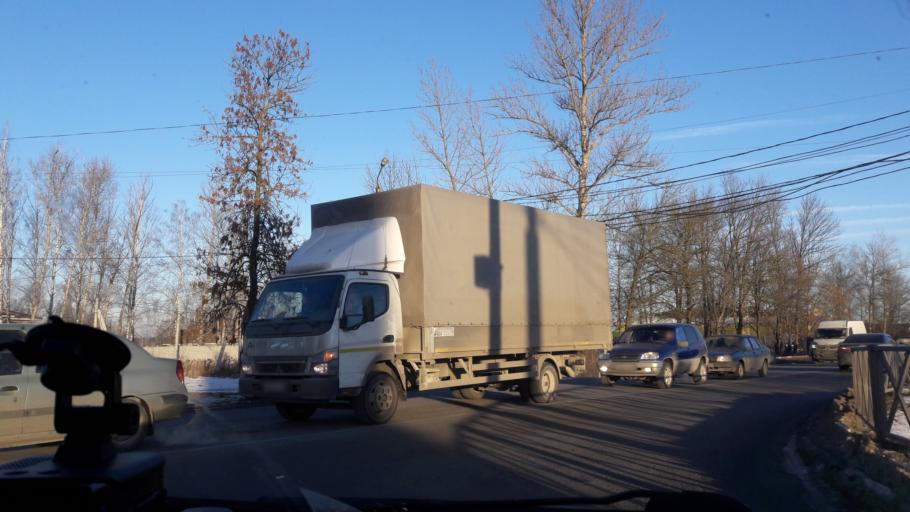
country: RU
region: Tula
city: Gorelki
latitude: 54.2415
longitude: 37.6187
